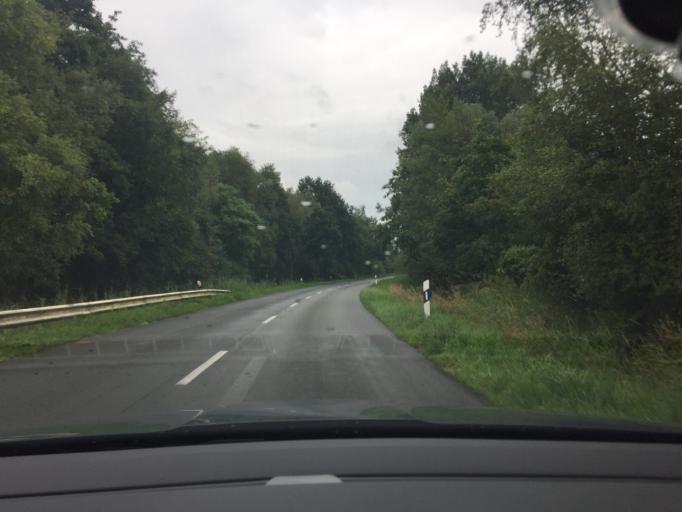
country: DE
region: Lower Saxony
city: Jemgum
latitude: 53.3686
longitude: 7.3999
